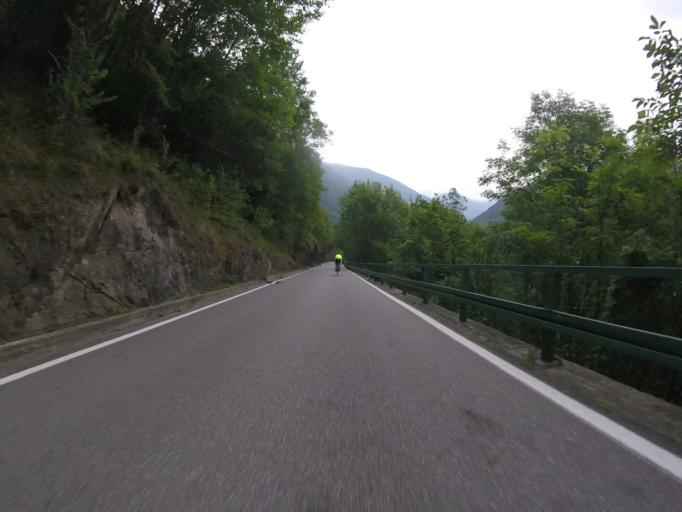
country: IT
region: Lombardy
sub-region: Provincia di Brescia
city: Monno
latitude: 46.2098
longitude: 10.3486
